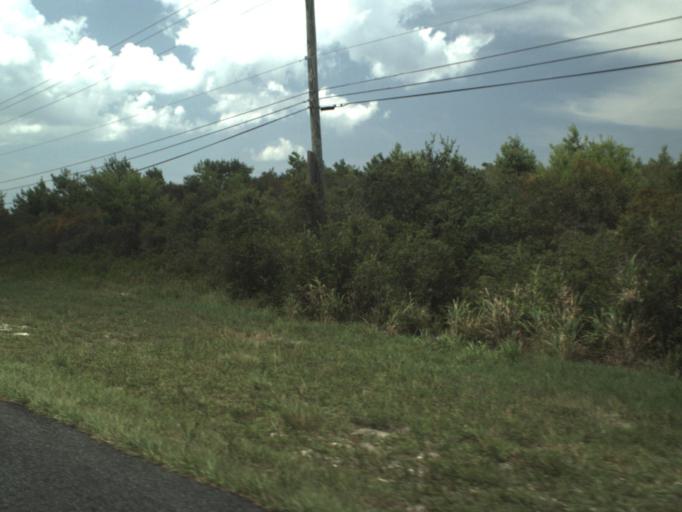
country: US
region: Florida
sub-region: Palm Beach County
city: Tequesta
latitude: 27.0153
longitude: -80.1049
